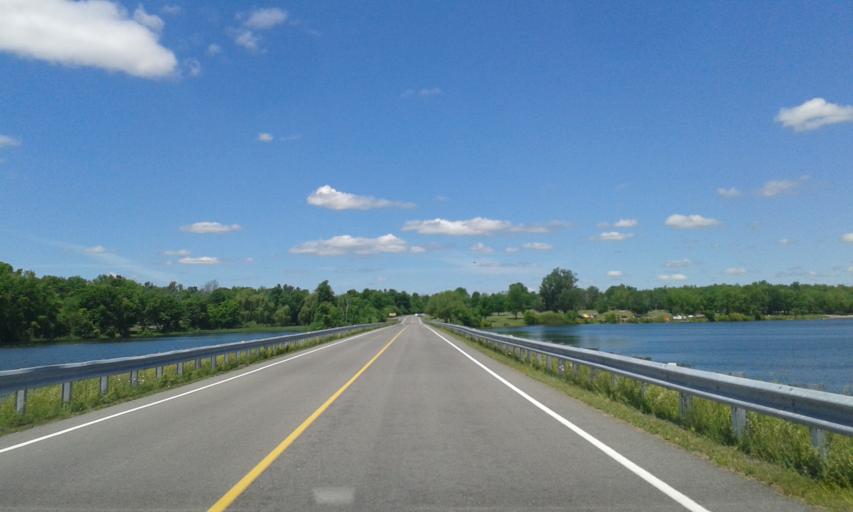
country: US
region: New York
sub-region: St. Lawrence County
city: Massena
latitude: 45.0077
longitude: -74.8945
